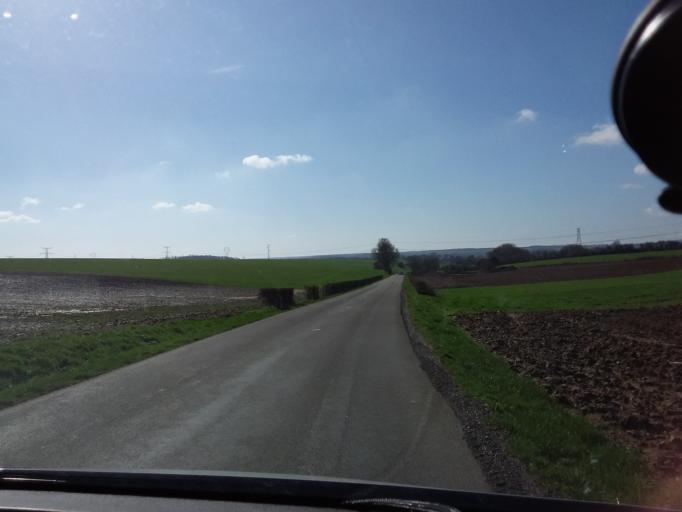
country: FR
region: Picardie
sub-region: Departement de l'Aisne
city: Hirson
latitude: 49.8910
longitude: 4.0984
